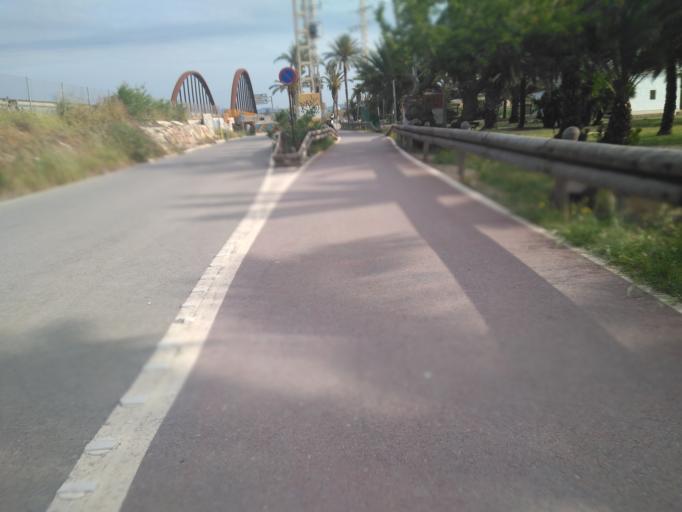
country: ES
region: Valencia
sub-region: Provincia de Valencia
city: Alboraya
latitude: 39.5009
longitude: -0.3254
